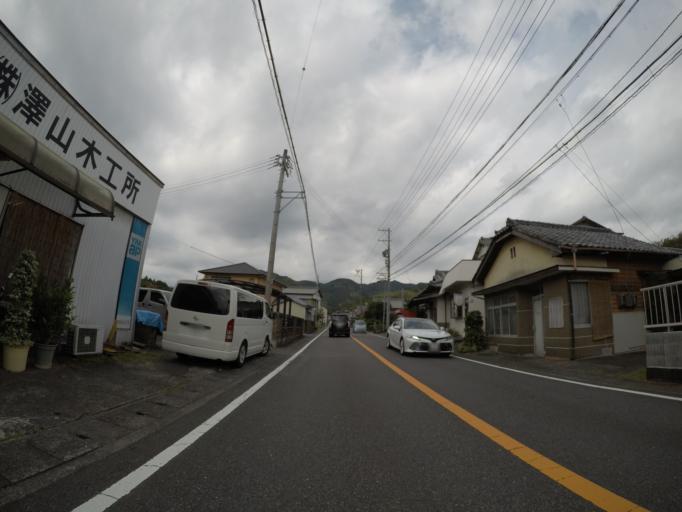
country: JP
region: Shizuoka
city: Fujieda
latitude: 34.8920
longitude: 138.2156
